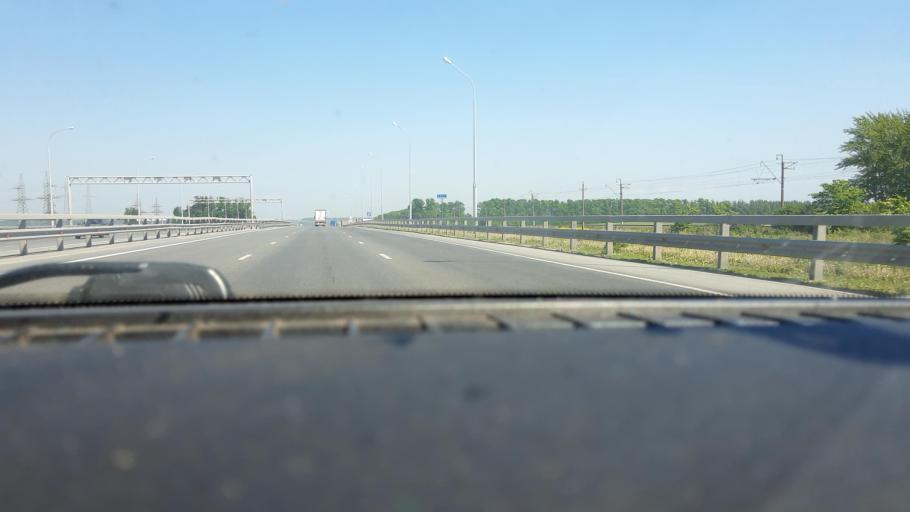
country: RU
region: Bashkortostan
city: Kabakovo
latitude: 54.6551
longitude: 56.1171
